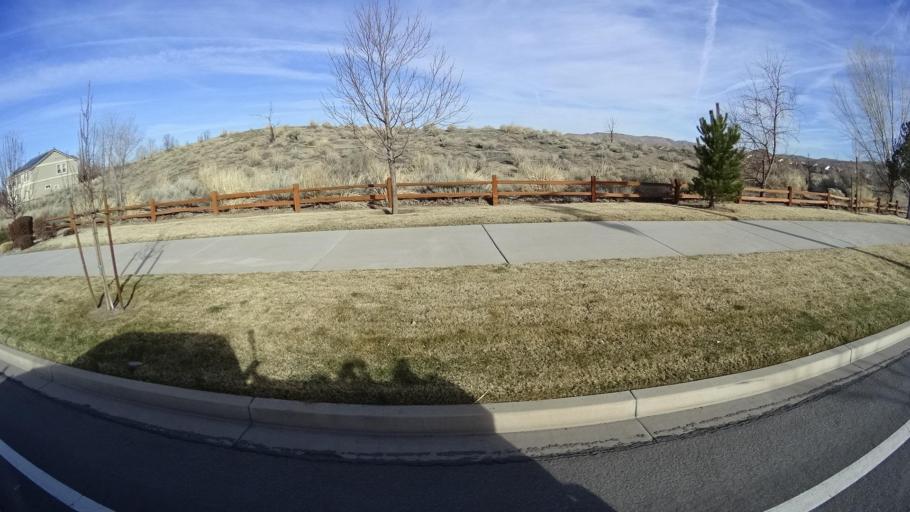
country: US
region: Nevada
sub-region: Washoe County
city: Spanish Springs
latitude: 39.6090
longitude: -119.6717
